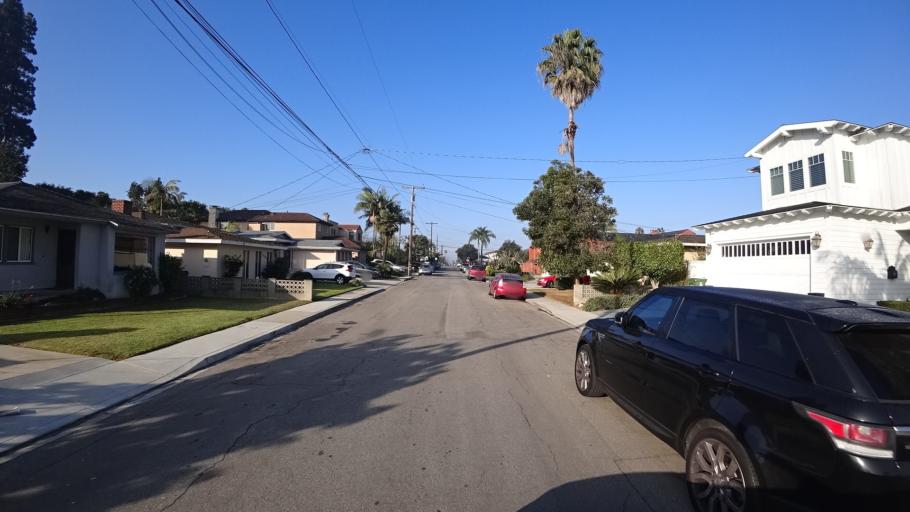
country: US
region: California
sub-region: Los Angeles County
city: Manhattan Beach
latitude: 33.8856
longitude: -118.3886
